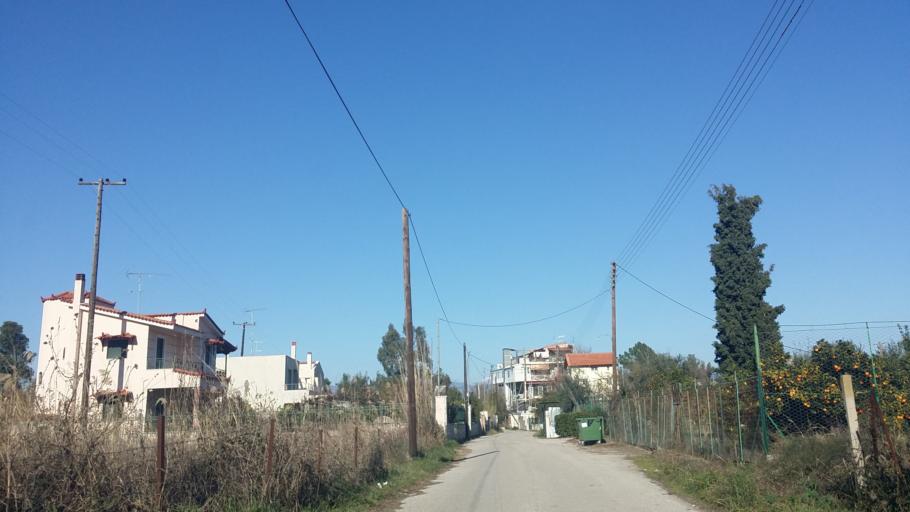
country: GR
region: West Greece
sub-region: Nomos Achaias
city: Temeni
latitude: 38.1988
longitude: 22.1798
